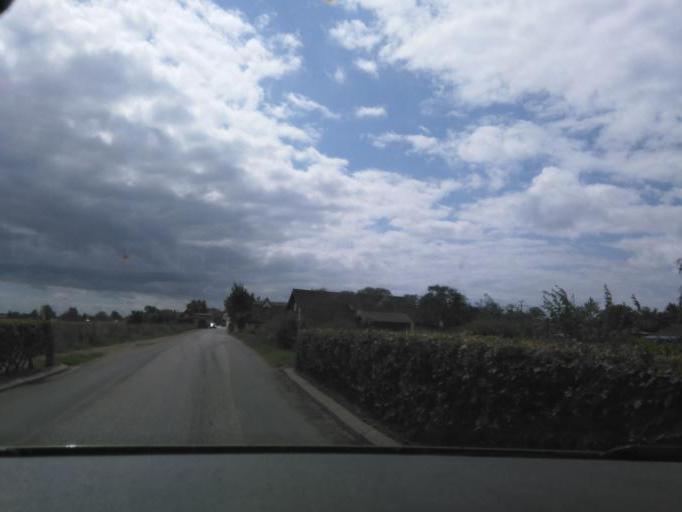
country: DK
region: Zealand
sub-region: Kalundborg Kommune
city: Gorlev
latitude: 55.5296
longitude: 11.1137
